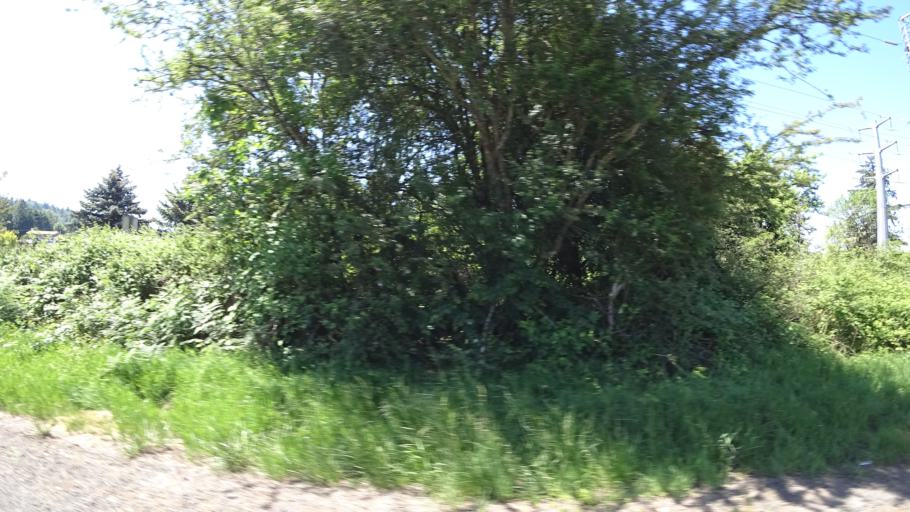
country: US
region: Oregon
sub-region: Clackamas County
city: Happy Valley
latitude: 45.4606
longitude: -122.4861
